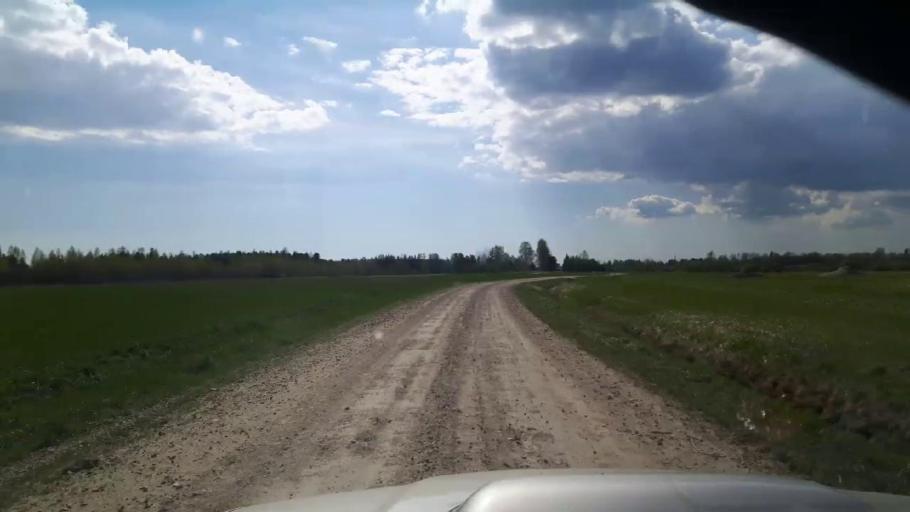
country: EE
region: Paernumaa
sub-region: Sindi linn
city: Sindi
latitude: 58.4242
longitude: 24.7508
